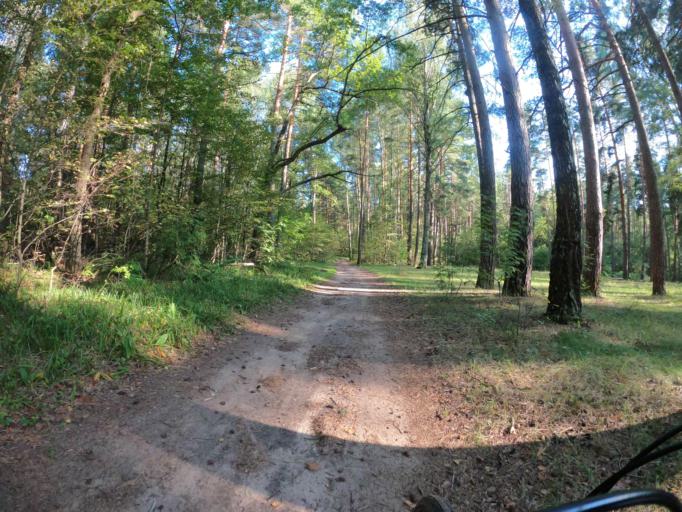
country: RU
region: Moskovskaya
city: Stupino
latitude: 54.8717
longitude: 38.0984
